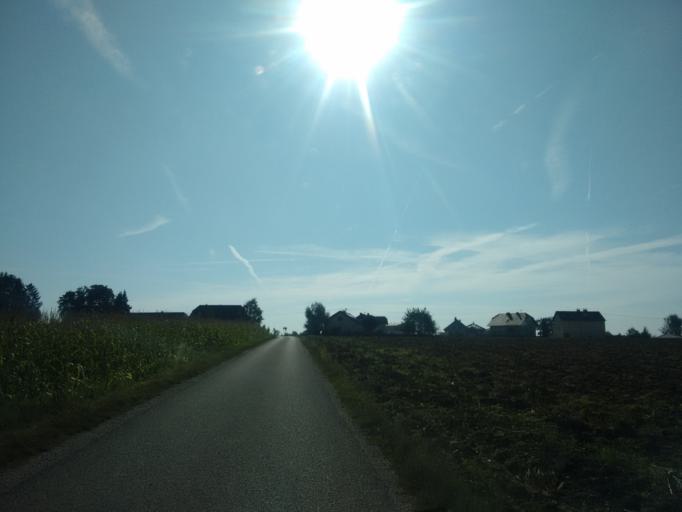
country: AT
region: Upper Austria
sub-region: Politischer Bezirk Steyr-Land
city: Bad Hall
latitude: 48.1334
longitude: 14.2071
